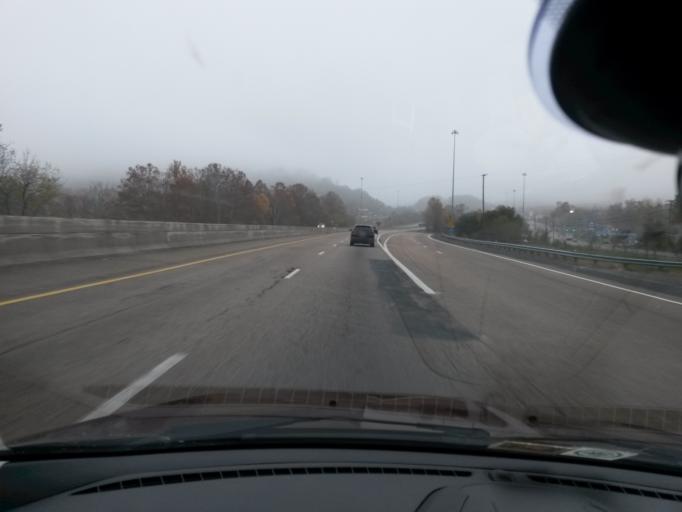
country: US
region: Virginia
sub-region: City of Covington
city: Fairlawn
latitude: 37.7722
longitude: -79.9622
